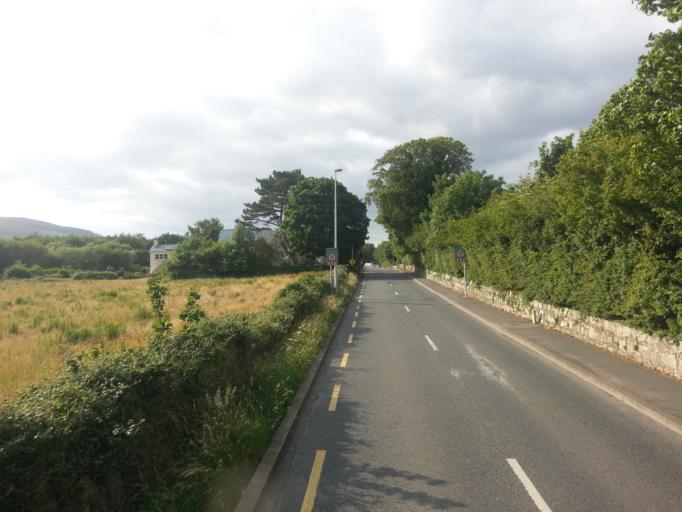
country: IE
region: Leinster
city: Foxrock
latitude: 53.2310
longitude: -6.1878
